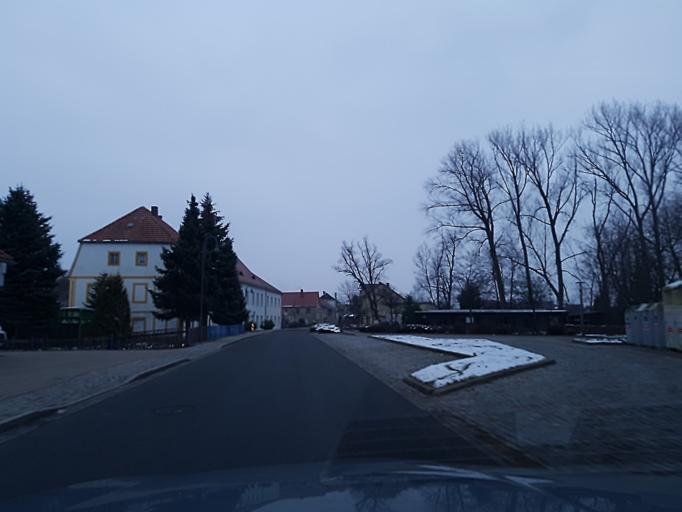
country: DE
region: Saxony
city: Stauchitz
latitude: 51.2477
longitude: 13.2092
